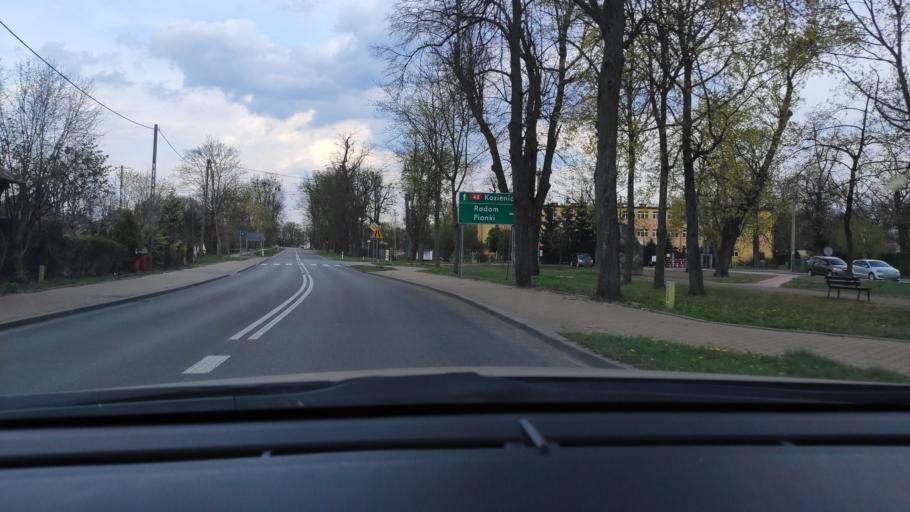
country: PL
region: Masovian Voivodeship
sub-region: Powiat kozienicki
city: Ryczywol
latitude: 51.6001
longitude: 21.3480
